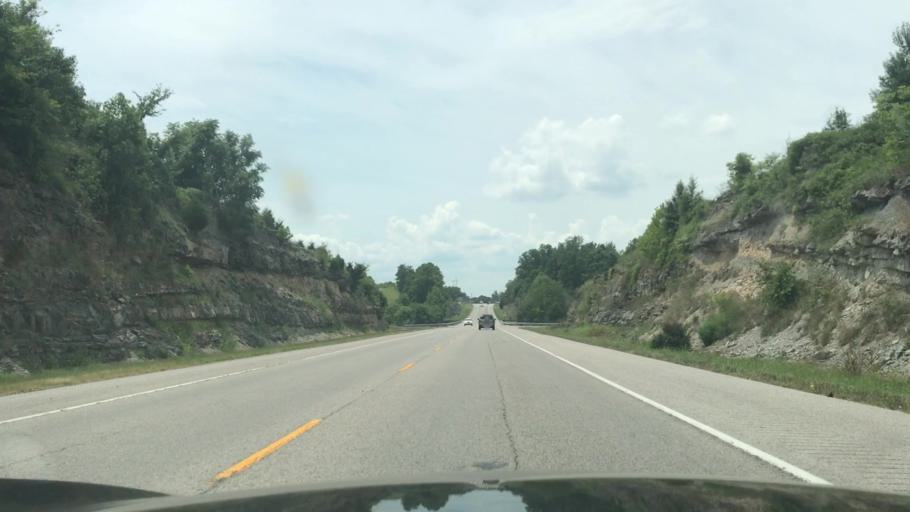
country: US
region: Kentucky
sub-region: Green County
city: Greensburg
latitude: 37.2790
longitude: -85.4909
